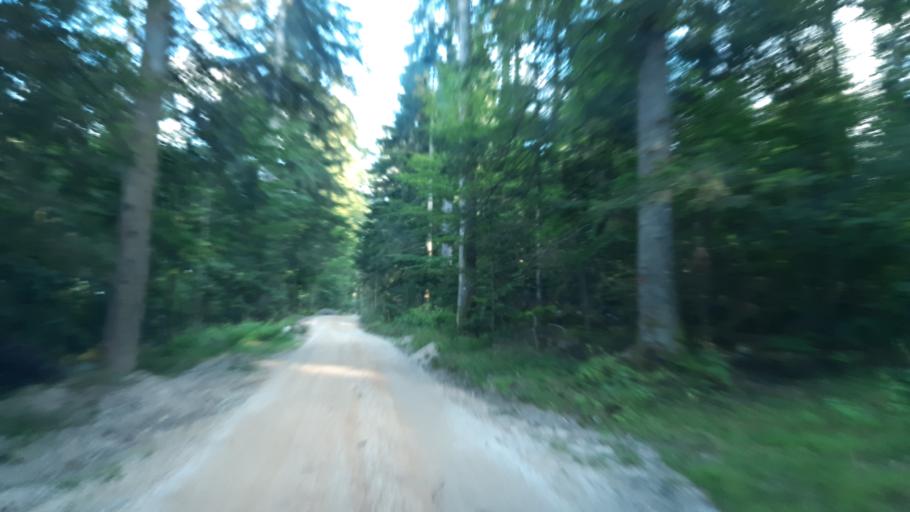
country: SI
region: Dolenjske Toplice
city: Dolenjske Toplice
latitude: 45.6968
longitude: 15.0115
